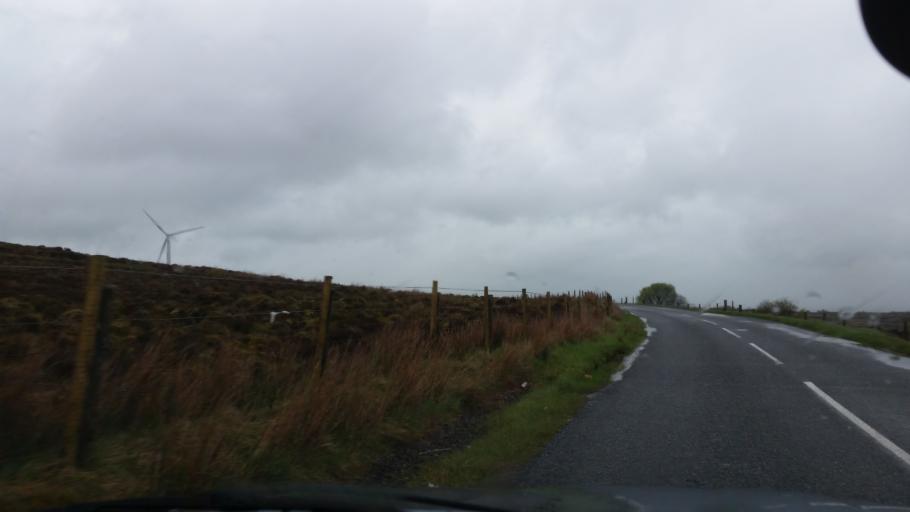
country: GB
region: Northern Ireland
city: Fintona
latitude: 54.4503
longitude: -7.3220
